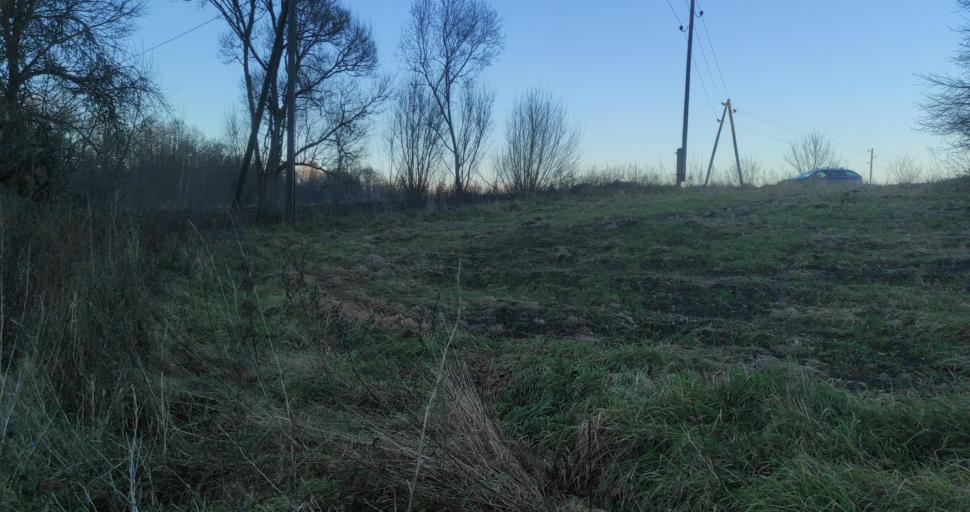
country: LV
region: Dundaga
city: Dundaga
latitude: 57.3847
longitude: 22.0871
